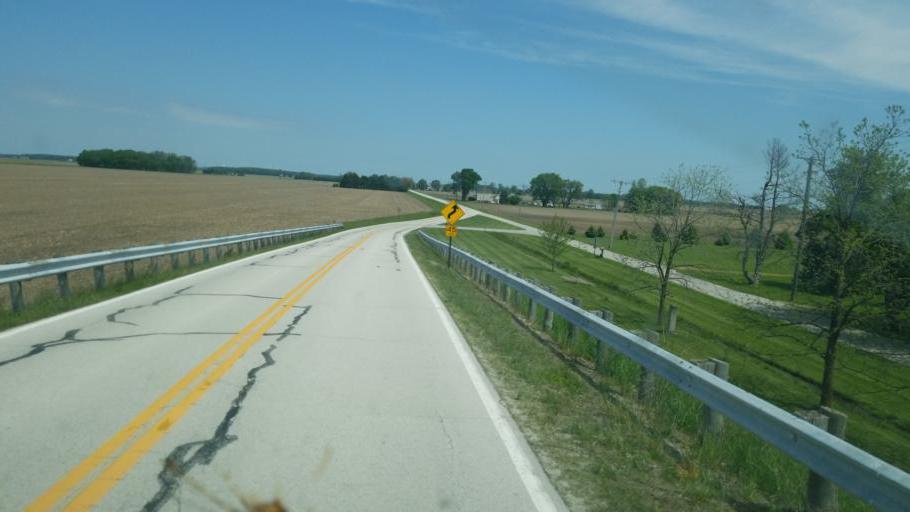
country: US
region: Ohio
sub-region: Sandusky County
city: Stony Prairie
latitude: 41.4308
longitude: -83.2018
